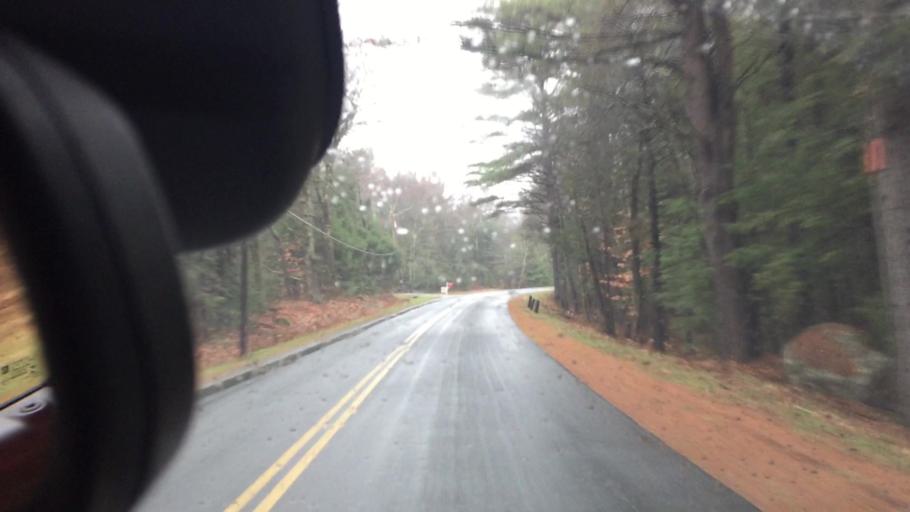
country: US
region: Massachusetts
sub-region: Berkshire County
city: Otis
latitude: 42.1898
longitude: -73.0323
